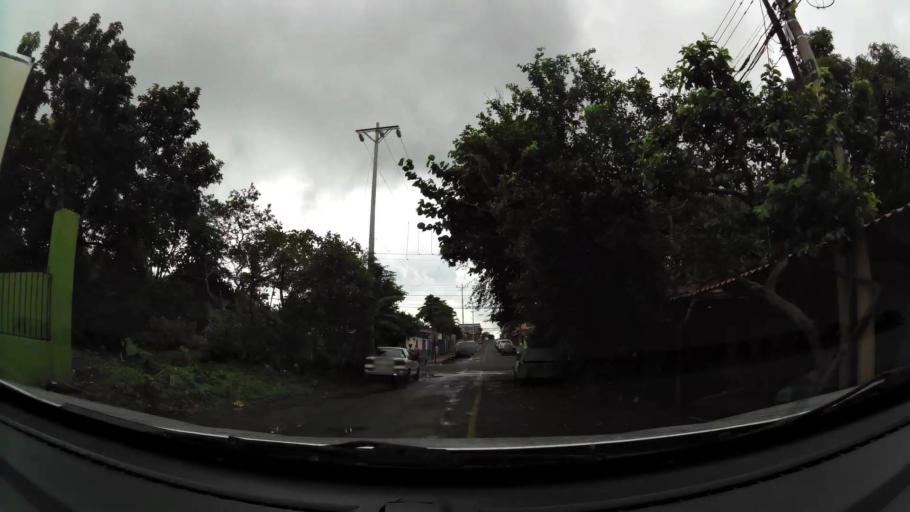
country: CR
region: Puntarenas
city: Esparza
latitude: 9.9931
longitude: -84.6678
